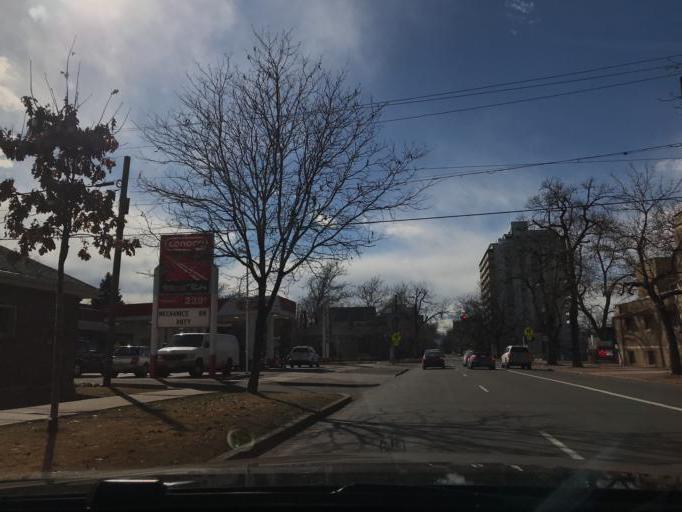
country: US
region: Colorado
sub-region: Denver County
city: Denver
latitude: 39.7290
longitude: -104.9721
